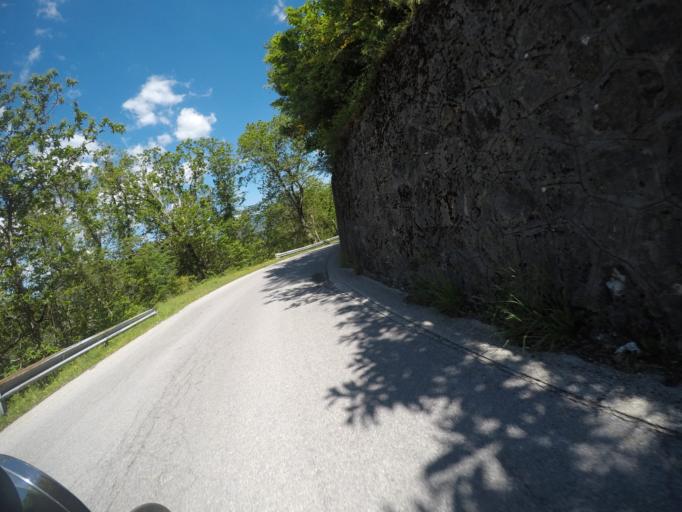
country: IT
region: Tuscany
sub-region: Provincia di Lucca
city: Careggine
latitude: 44.1301
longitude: 10.3358
